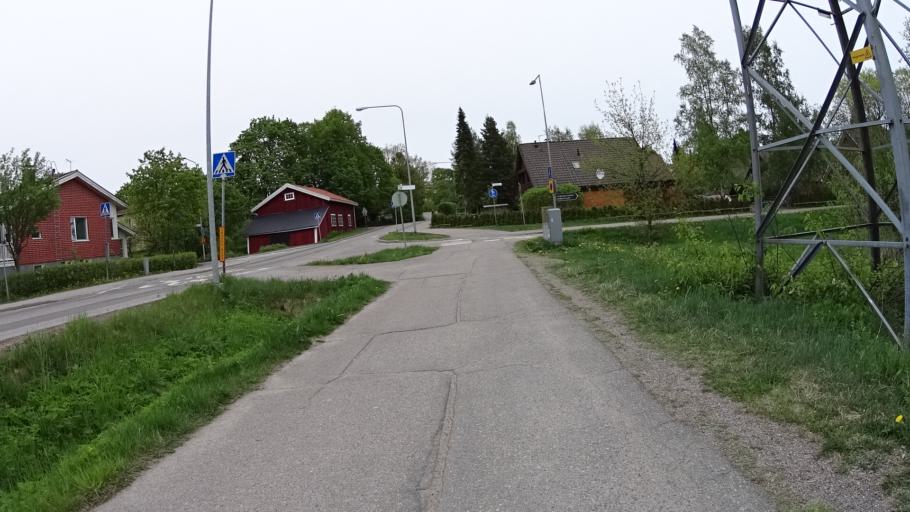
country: FI
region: Uusimaa
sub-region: Helsinki
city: Kilo
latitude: 60.2667
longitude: 24.7898
